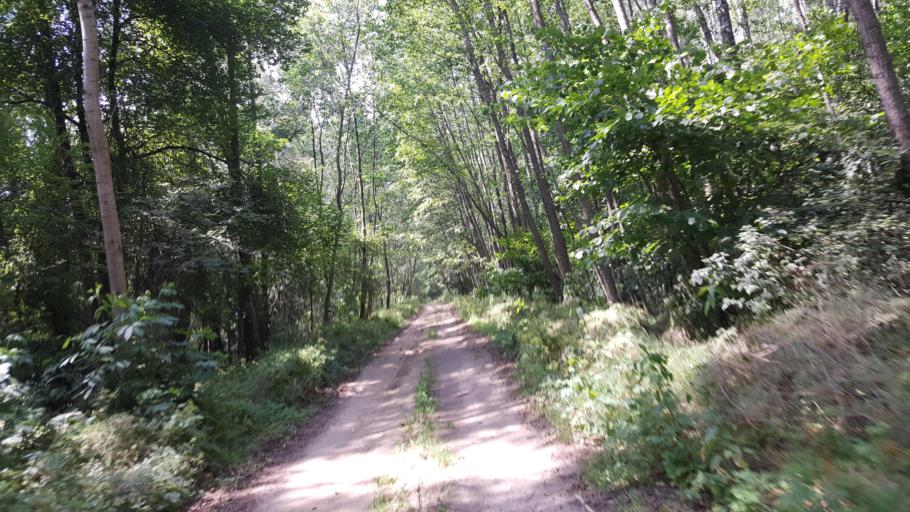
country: BY
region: Brest
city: Kamyanyets
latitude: 52.3658
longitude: 23.7555
